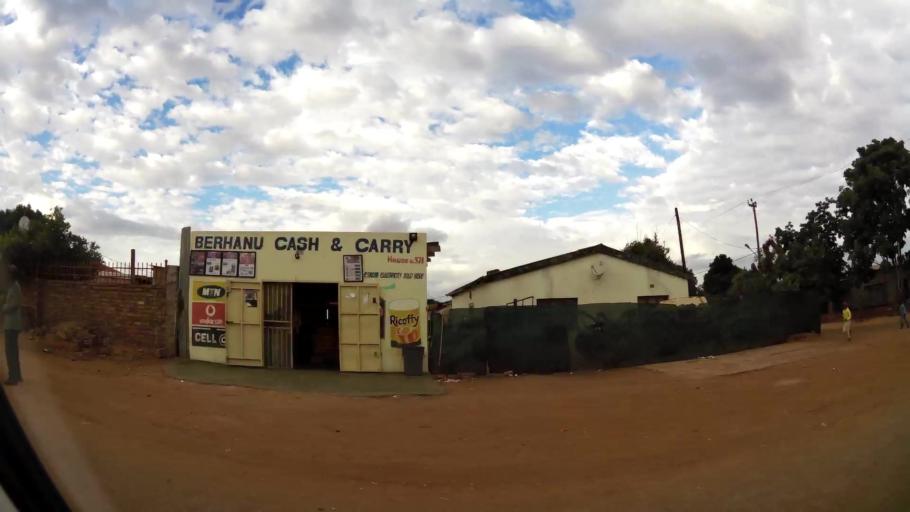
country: ZA
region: Limpopo
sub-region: Waterberg District Municipality
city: Modimolle
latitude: -24.5243
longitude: 28.7228
